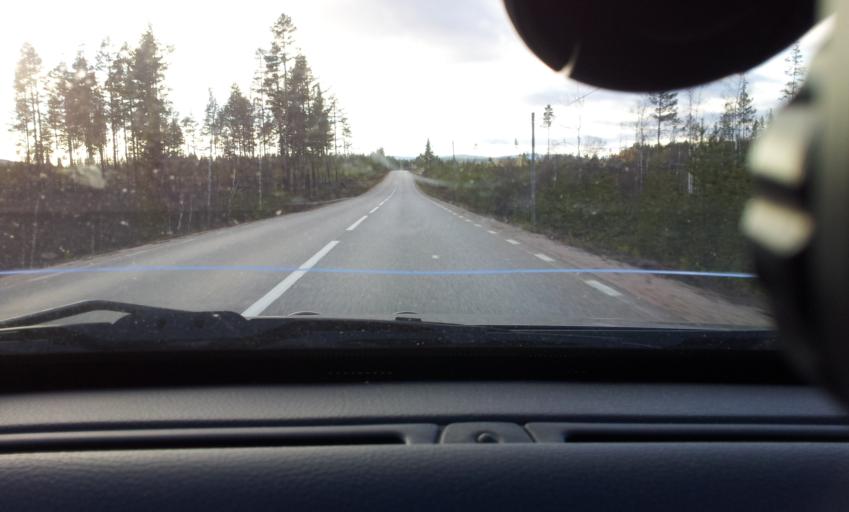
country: SE
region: Jaemtland
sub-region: Harjedalens Kommun
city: Sveg
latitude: 62.1257
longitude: 14.9841
